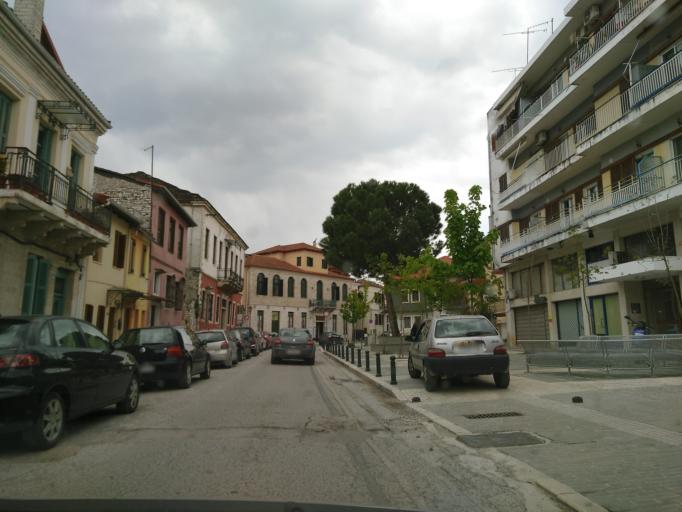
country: GR
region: Epirus
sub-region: Nomos Ioanninon
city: Ioannina
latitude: 39.6709
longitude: 20.8556
